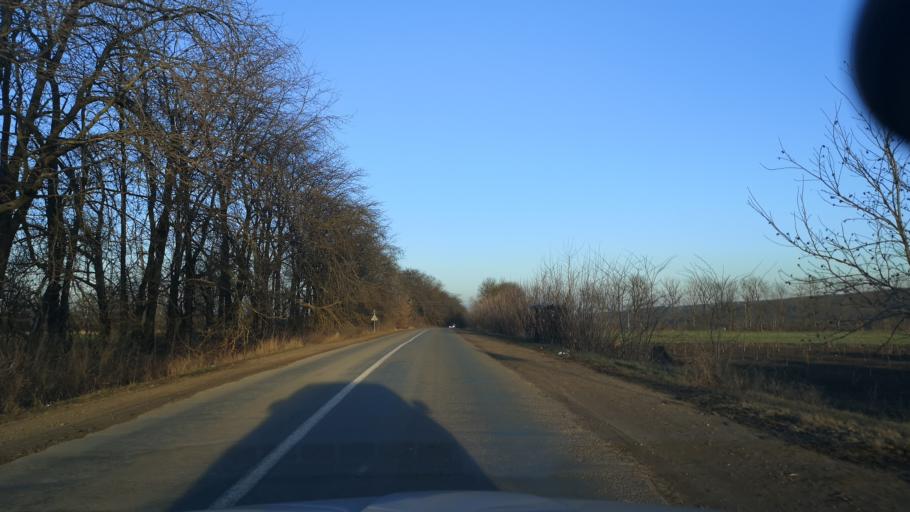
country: MD
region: Orhei
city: Orhei
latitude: 47.2870
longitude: 28.8788
